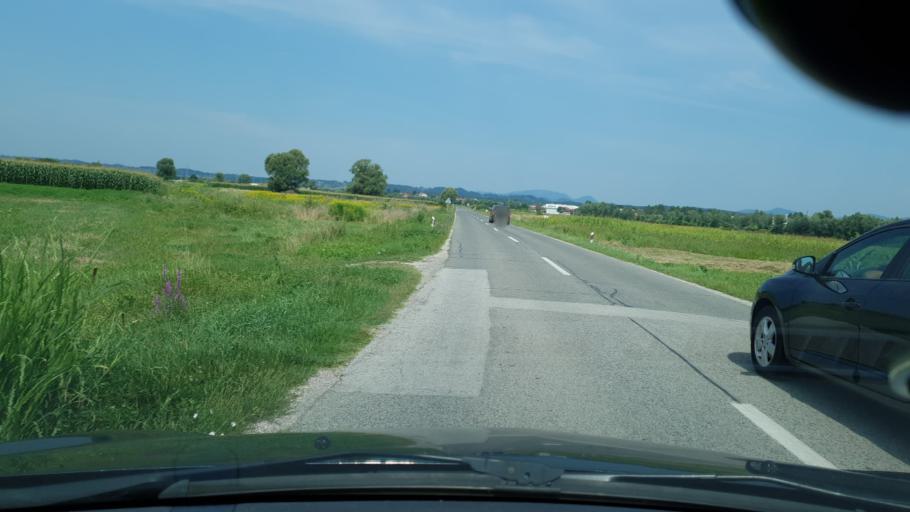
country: HR
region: Krapinsko-Zagorska
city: Marija Bistrica
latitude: 46.0366
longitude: 16.0886
